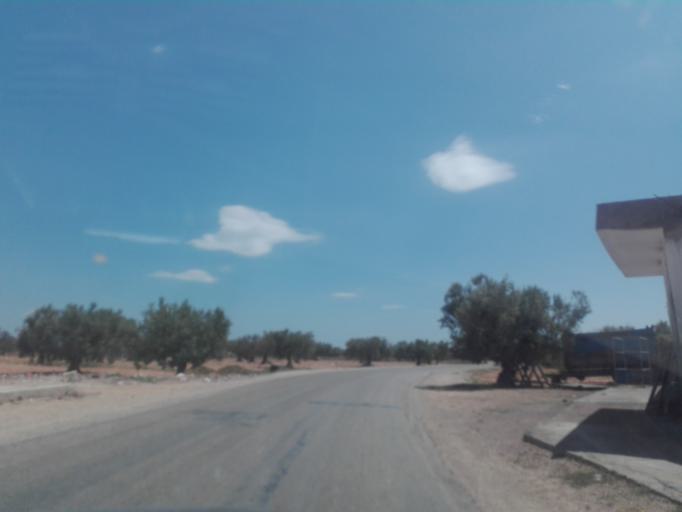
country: TN
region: Safaqis
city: Sfax
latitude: 34.6226
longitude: 10.6103
